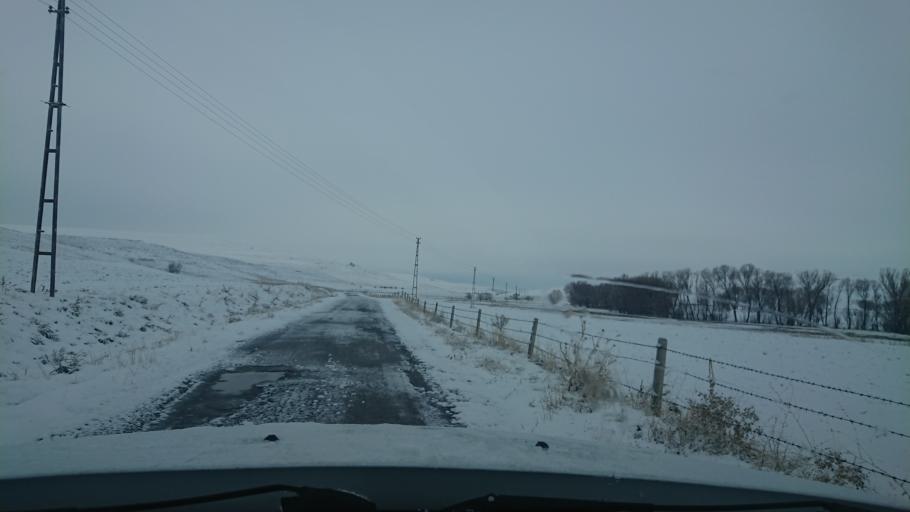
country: TR
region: Aksaray
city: Acipinar
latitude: 38.6790
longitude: 33.8661
